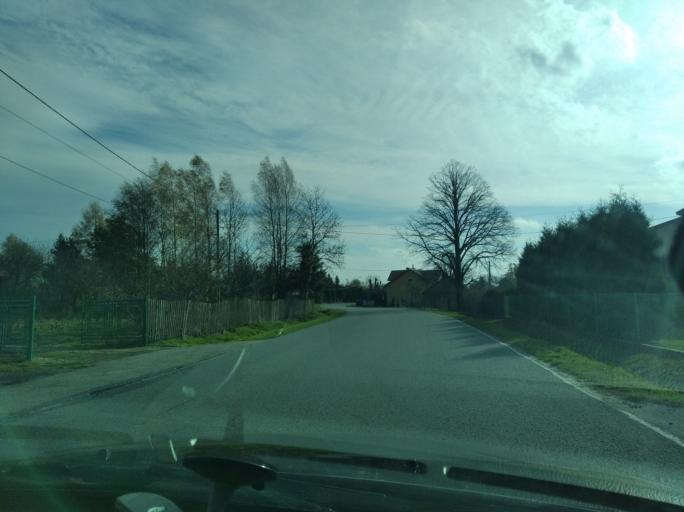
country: PL
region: Subcarpathian Voivodeship
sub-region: Powiat ropczycko-sedziszowski
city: Sedziszow Malopolski
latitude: 50.0873
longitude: 21.7488
